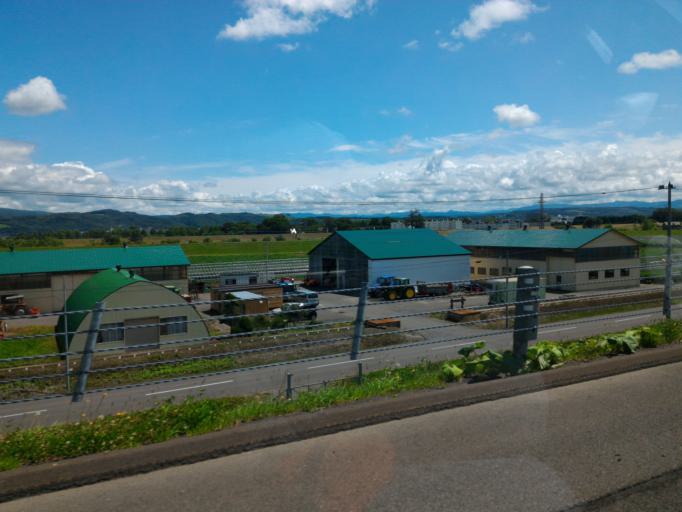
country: JP
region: Hokkaido
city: Nayoro
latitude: 44.3588
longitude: 142.4358
